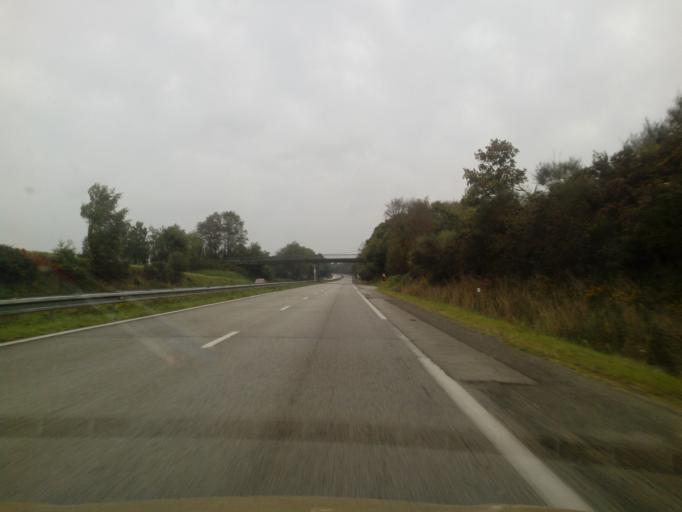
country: FR
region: Brittany
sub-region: Departement du Morbihan
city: Branderion
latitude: 47.8086
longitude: -3.2303
